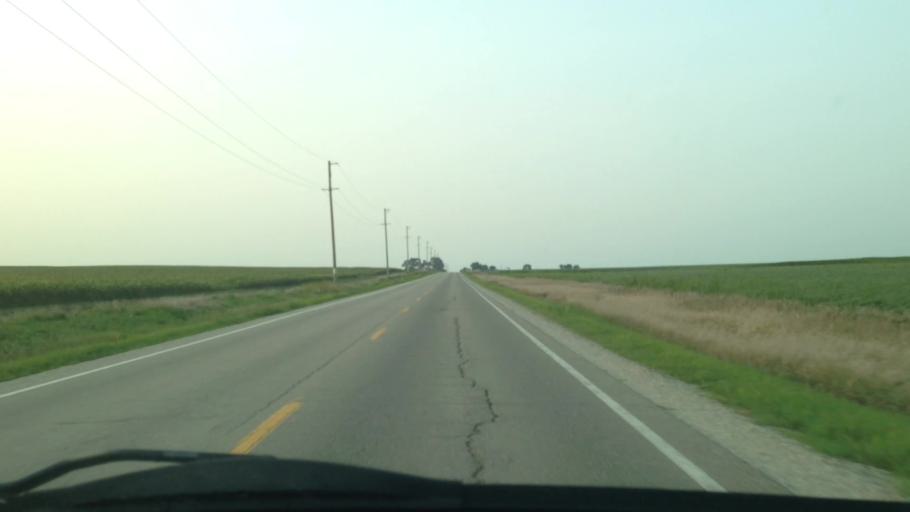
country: US
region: Iowa
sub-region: Iowa County
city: Marengo
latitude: 41.9536
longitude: -92.0852
